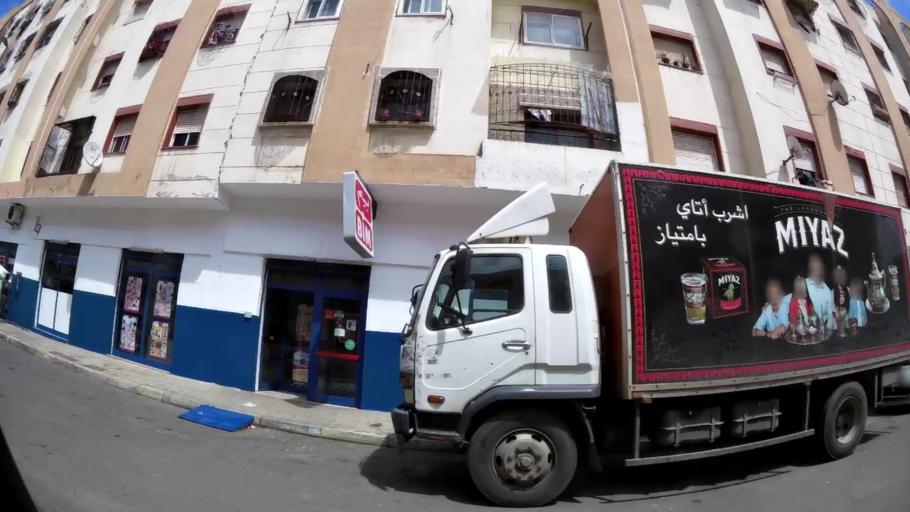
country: MA
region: Grand Casablanca
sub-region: Mediouna
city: Tit Mellil
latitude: 33.6025
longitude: -7.4811
